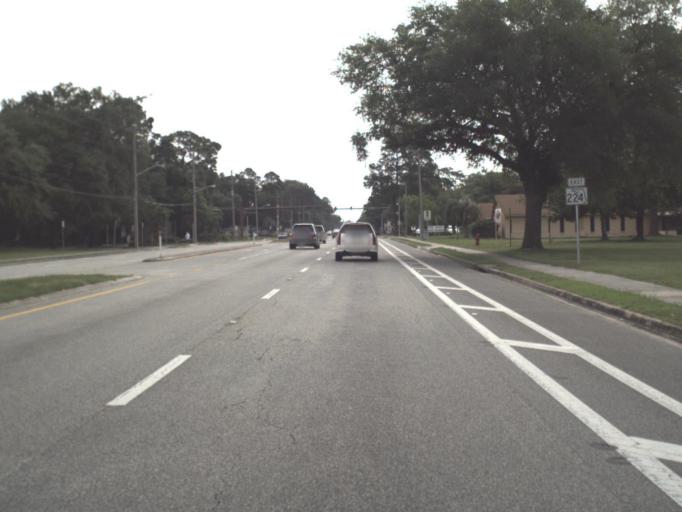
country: US
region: Florida
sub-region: Clay County
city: Orange Park
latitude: 30.1652
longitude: -81.7231
